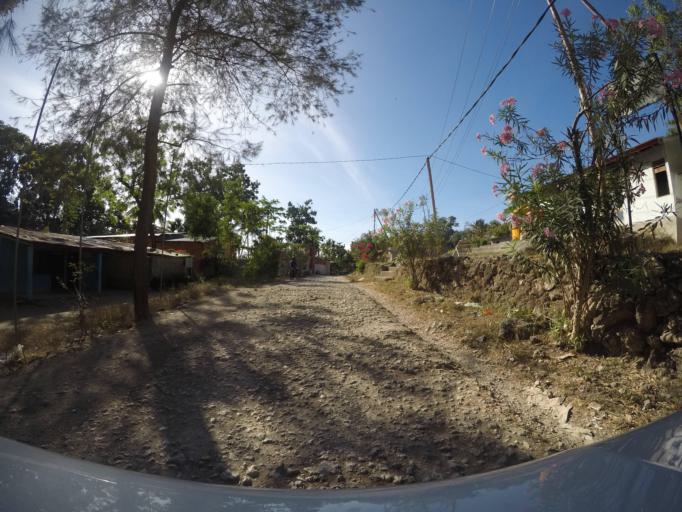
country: TL
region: Baucau
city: Baucau
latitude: -8.4528
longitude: 126.4372
